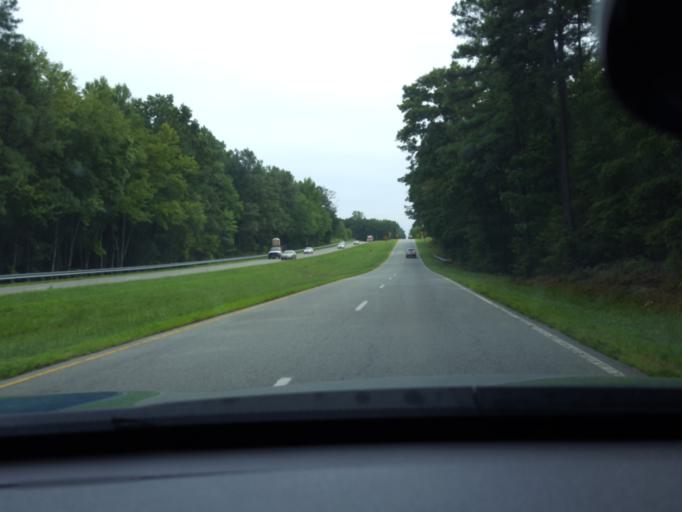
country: US
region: Virginia
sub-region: Caroline County
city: Bowling Green
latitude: 38.0045
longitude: -77.3343
